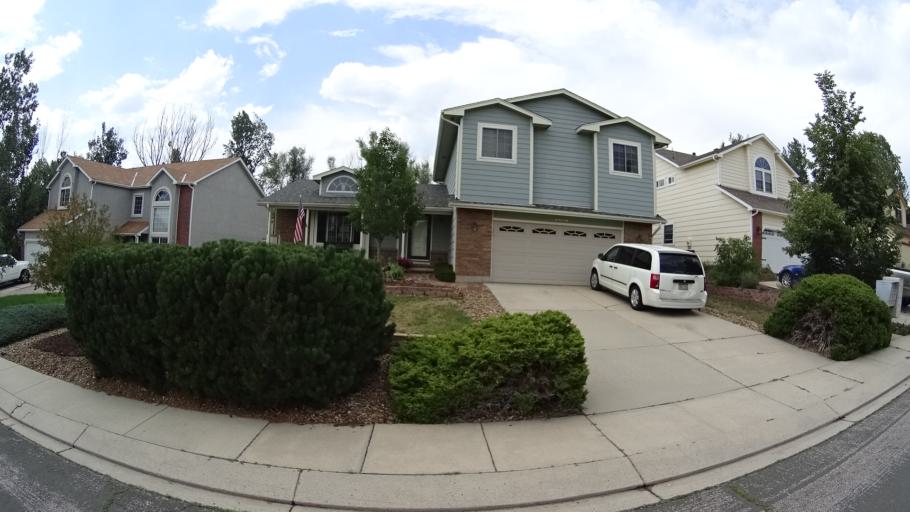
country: US
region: Colorado
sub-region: El Paso County
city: Black Forest
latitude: 38.9595
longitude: -104.7405
